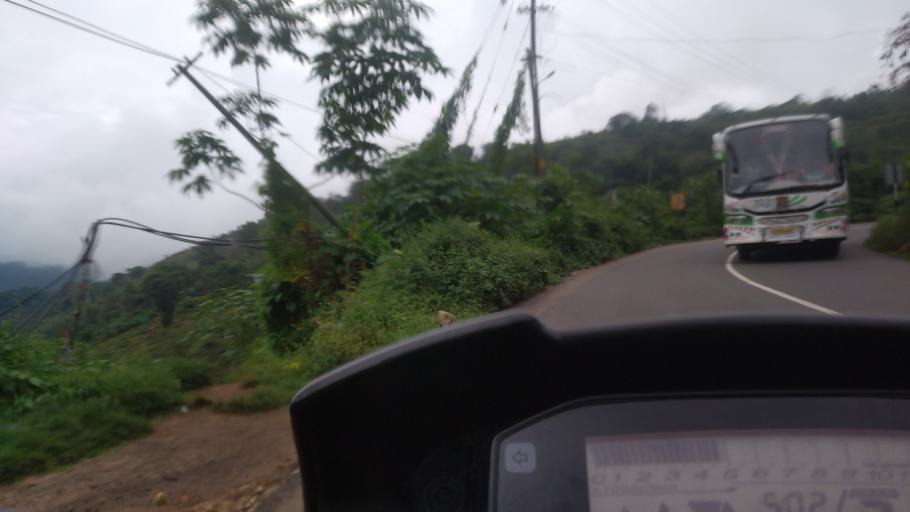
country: IN
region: Tamil Nadu
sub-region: Theni
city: Gudalur
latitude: 9.5760
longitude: 77.0554
